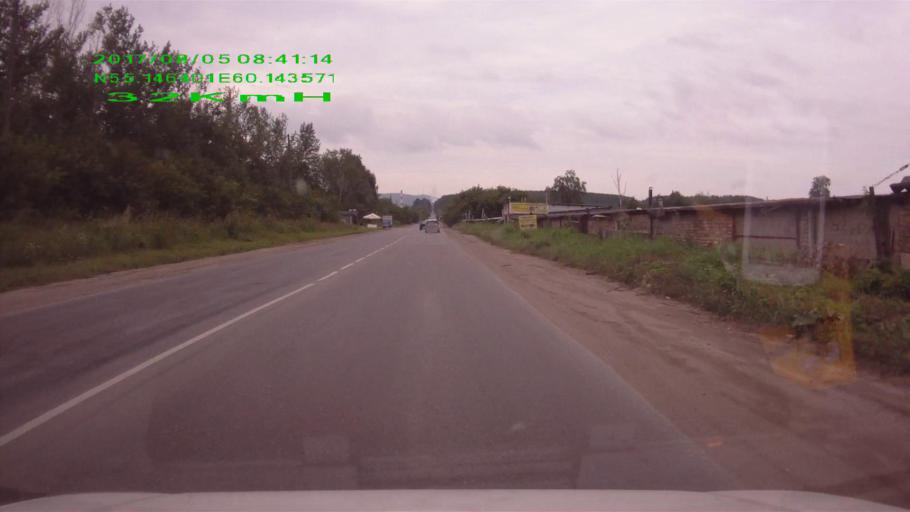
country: RU
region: Chelyabinsk
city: Turgoyak
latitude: 55.1462
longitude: 60.1436
